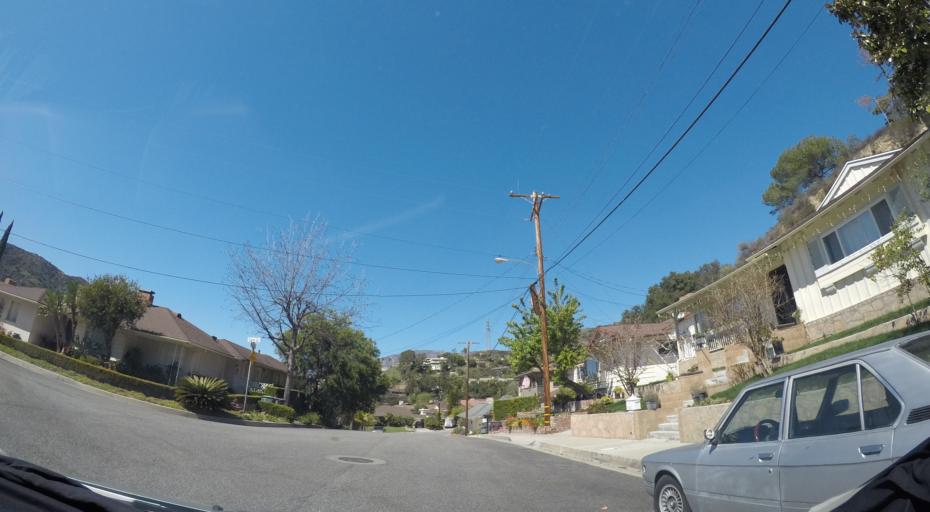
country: US
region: California
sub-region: Los Angeles County
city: La Canada Flintridge
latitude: 34.1809
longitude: -118.2241
